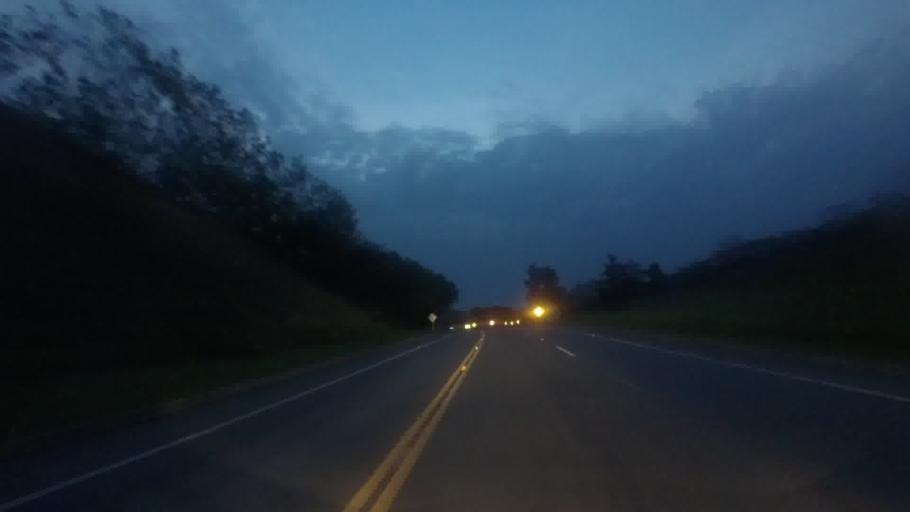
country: BR
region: Rio de Janeiro
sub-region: Sapucaia
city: Sapucaia
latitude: -21.9542
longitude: -42.8421
